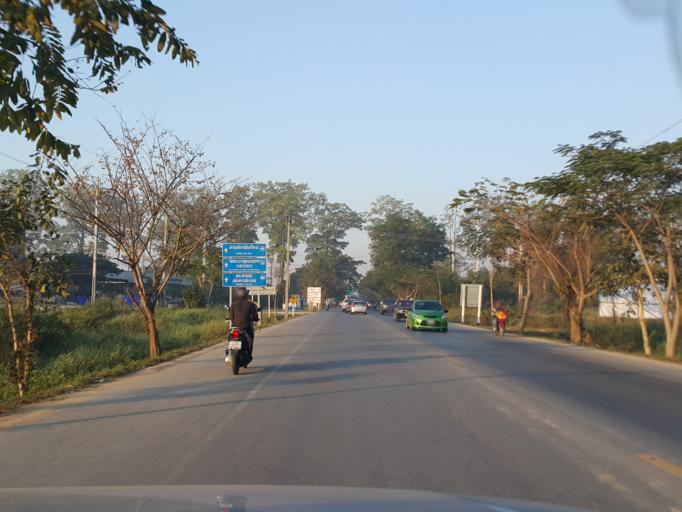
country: TH
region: Chiang Mai
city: Saraphi
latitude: 18.7303
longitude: 99.0256
